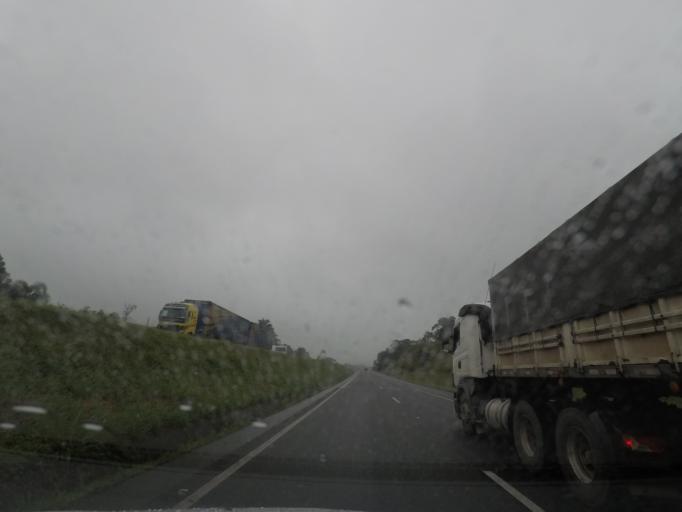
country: BR
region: Sao Paulo
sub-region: Cajati
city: Cajati
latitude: -24.9607
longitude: -48.3381
